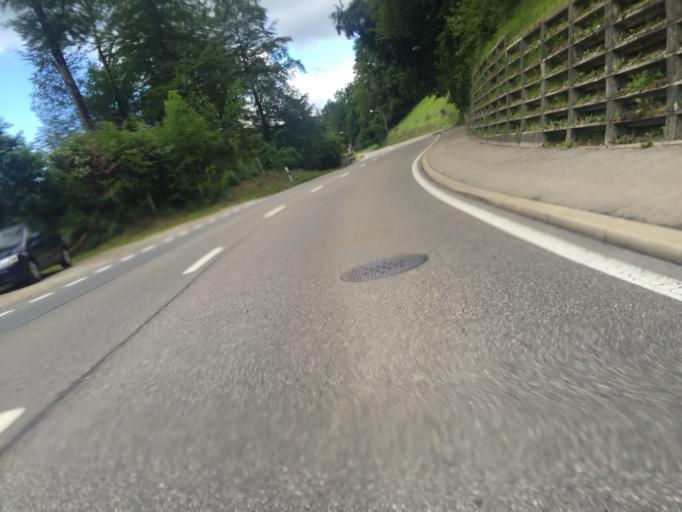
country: CH
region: Bern
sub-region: Bern-Mittelland District
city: Wohlen
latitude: 46.9704
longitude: 7.3636
